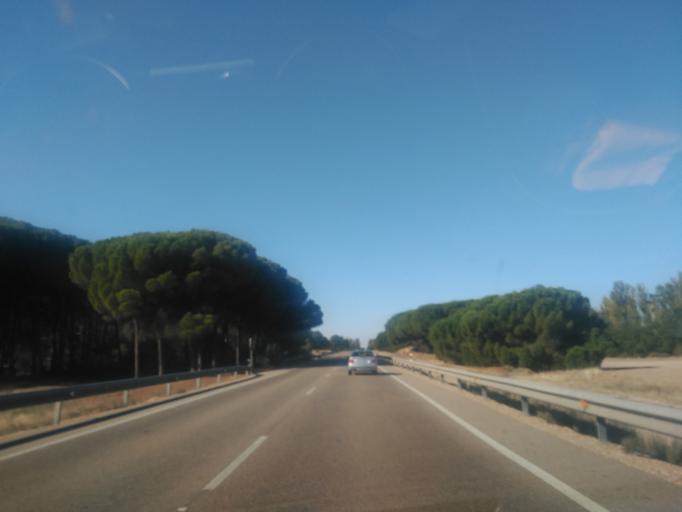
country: ES
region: Castille and Leon
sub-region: Provincia de Valladolid
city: Sardon de Duero
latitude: 41.6043
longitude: -4.4560
